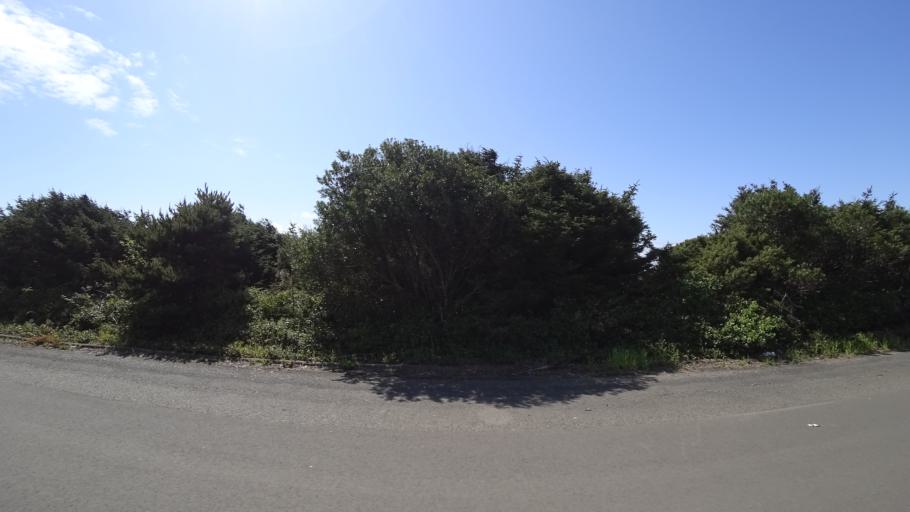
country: US
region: Oregon
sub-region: Lincoln County
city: Newport
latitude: 44.7184
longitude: -124.0584
